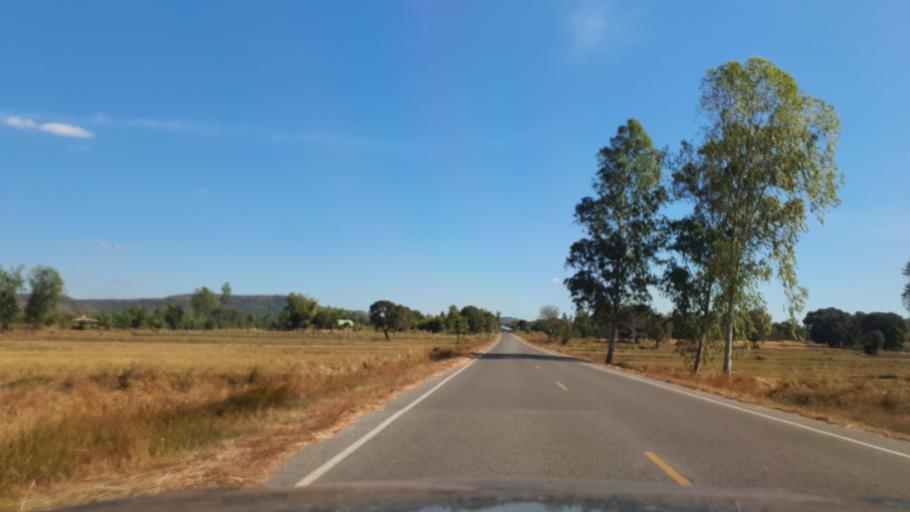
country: TH
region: Kalasin
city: Khao Wong
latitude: 16.7186
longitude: 104.1107
